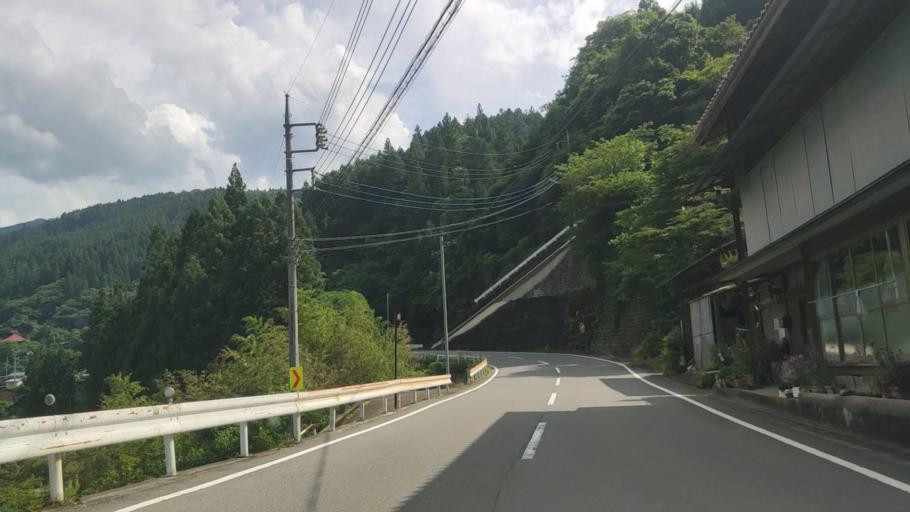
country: JP
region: Gunma
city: Tomioka
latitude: 36.1559
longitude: 138.7282
